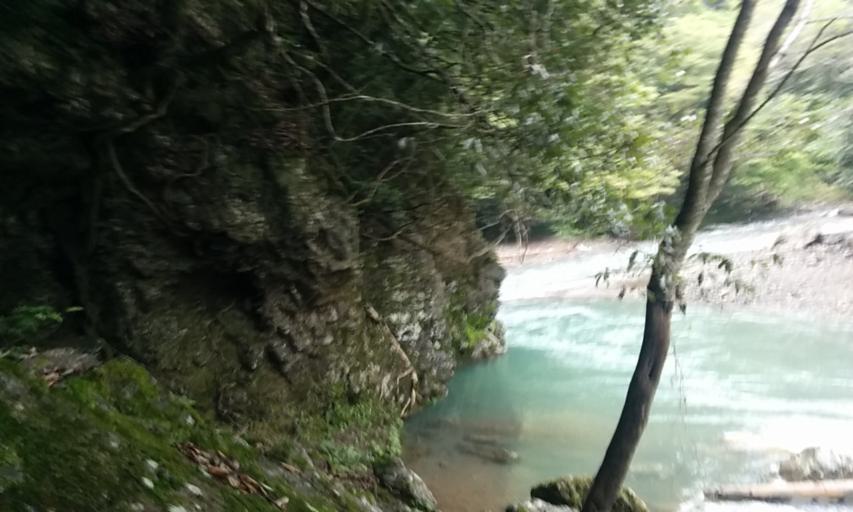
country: JP
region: Kyoto
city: Kameoka
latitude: 35.0498
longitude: 135.6620
